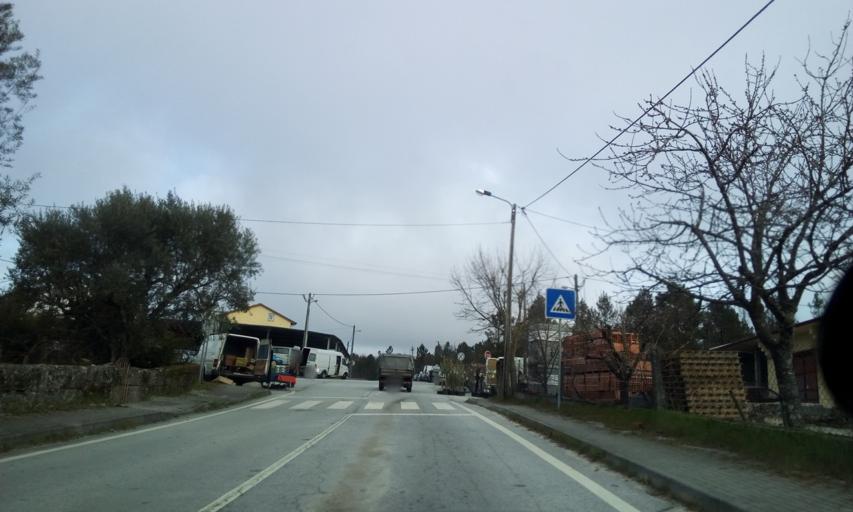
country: PT
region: Guarda
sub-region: Aguiar da Beira
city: Aguiar da Beira
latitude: 40.7239
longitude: -7.4932
